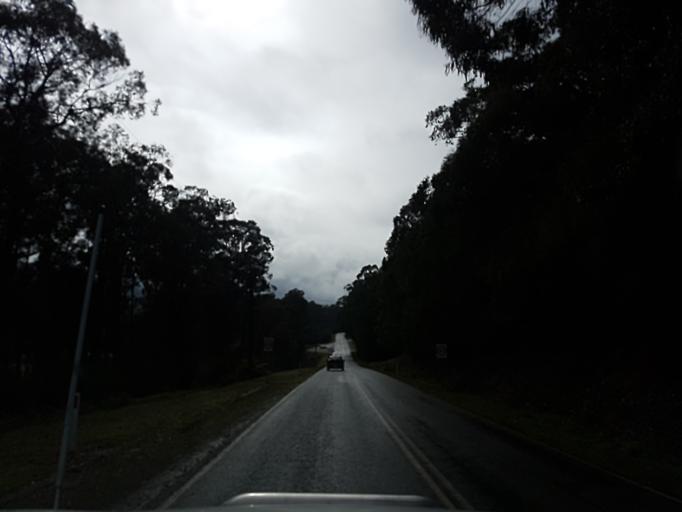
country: AU
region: Victoria
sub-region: Yarra Ranges
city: Millgrove
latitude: -37.7269
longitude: 145.7504
